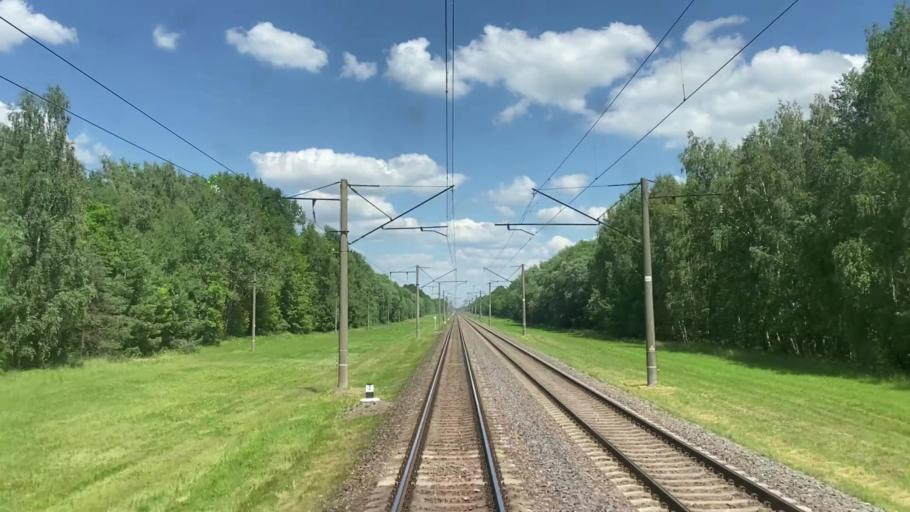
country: BY
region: Brest
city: Zhabinka
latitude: 52.2418
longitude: 24.1013
